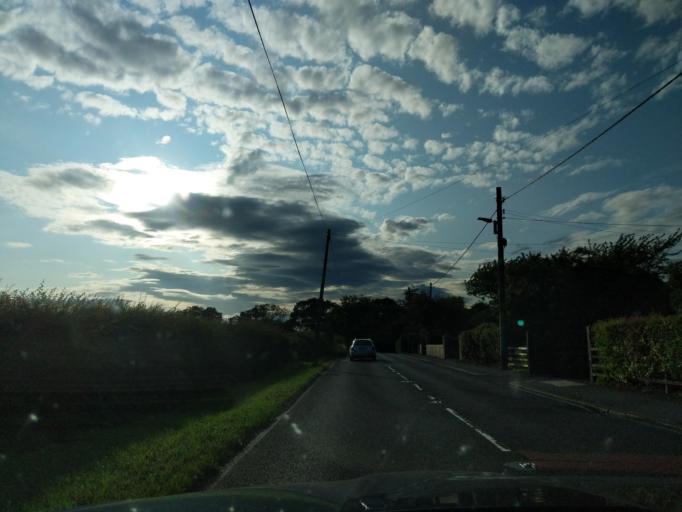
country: GB
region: England
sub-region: Northumberland
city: Bedlington
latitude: 55.1232
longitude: -1.5795
